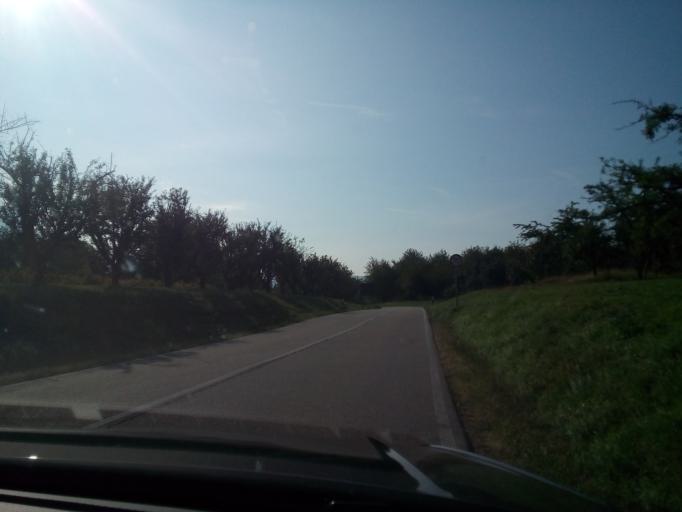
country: DE
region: Baden-Wuerttemberg
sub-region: Freiburg Region
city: Haslach
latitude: 48.5660
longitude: 8.0417
